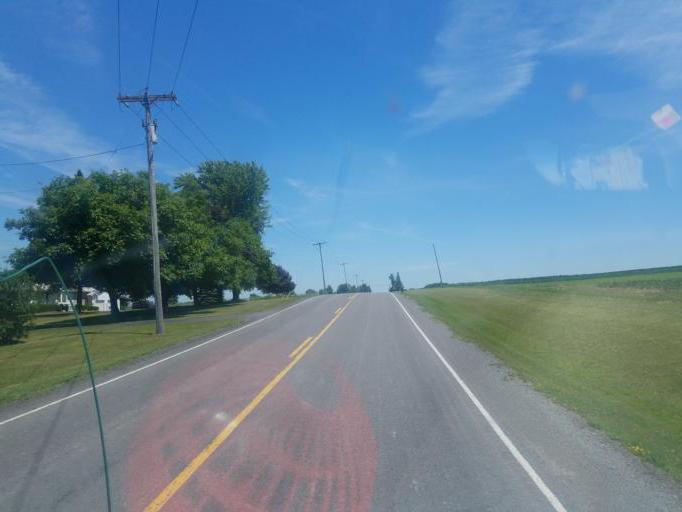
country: US
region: New York
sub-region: Yates County
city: Penn Yan
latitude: 42.6229
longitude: -76.9910
